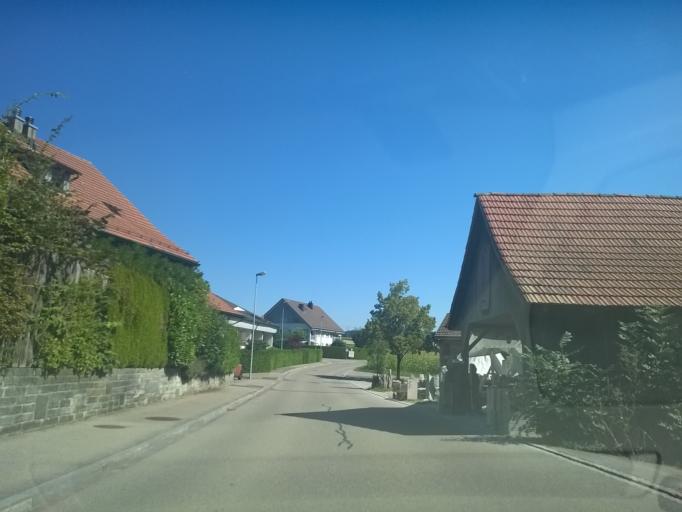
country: CH
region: Zurich
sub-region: Bezirk Buelach
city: Birchwil
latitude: 47.4645
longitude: 8.6415
